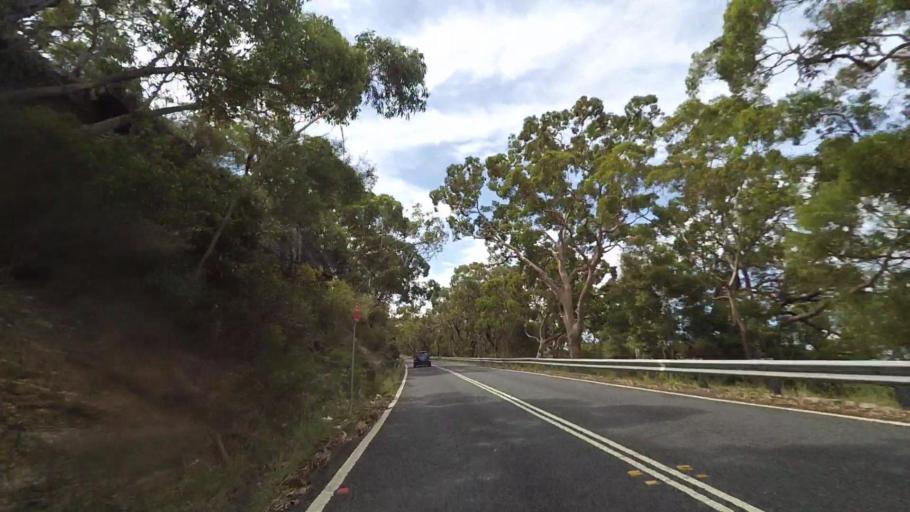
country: AU
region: New South Wales
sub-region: Sutherland Shire
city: Loftus
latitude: -34.0685
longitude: 151.0571
